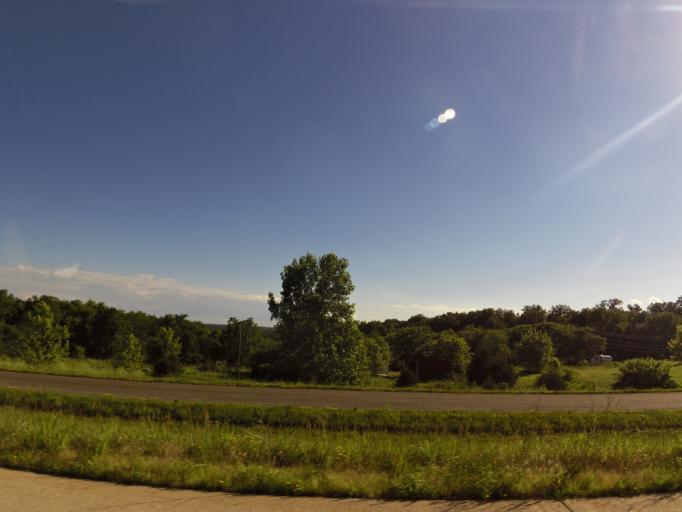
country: US
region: Missouri
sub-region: Ralls County
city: New London
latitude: 39.5262
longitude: -91.3503
